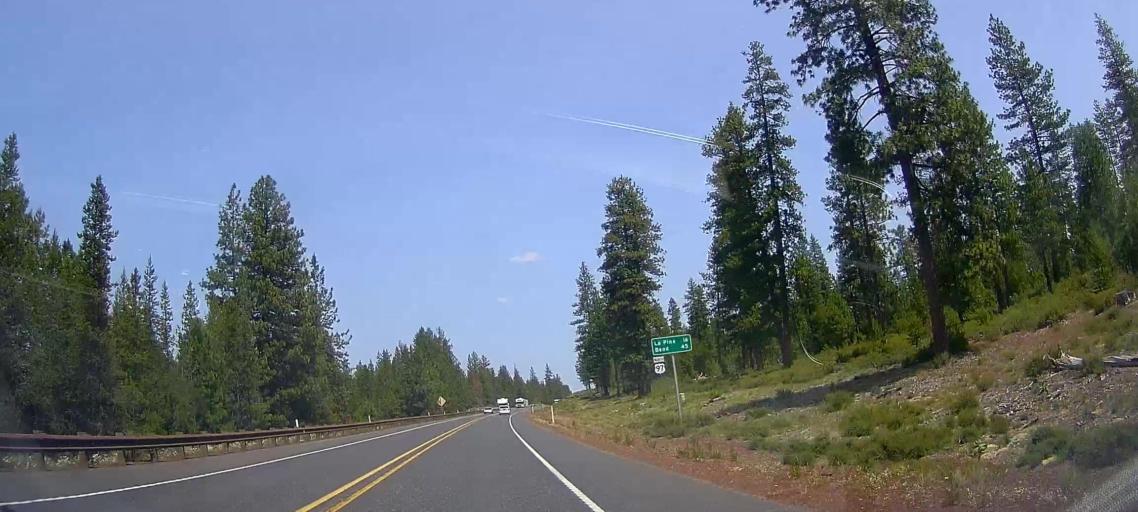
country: US
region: Oregon
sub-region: Deschutes County
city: La Pine
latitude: 43.4847
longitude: -121.6847
